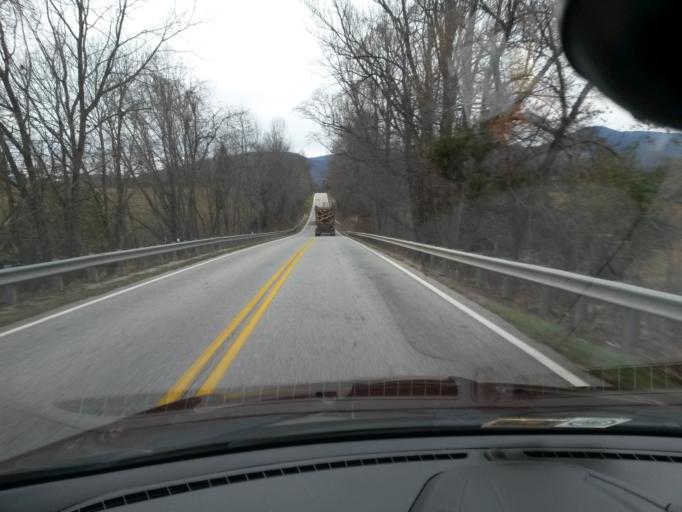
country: US
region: Virginia
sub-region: Amherst County
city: Amherst
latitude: 37.6526
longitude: -79.1359
